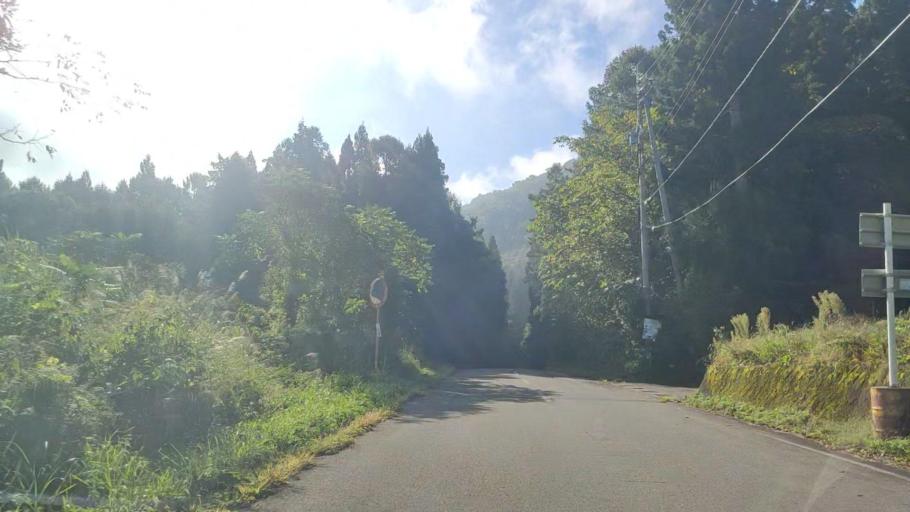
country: JP
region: Nagano
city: Iiyama
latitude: 36.8258
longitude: 138.4081
